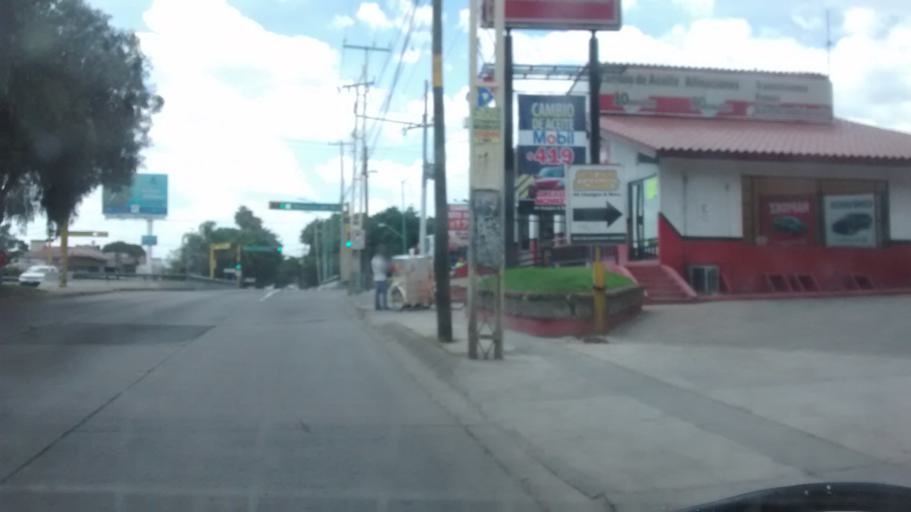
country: MX
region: Guanajuato
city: Leon
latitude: 21.1080
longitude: -101.6619
